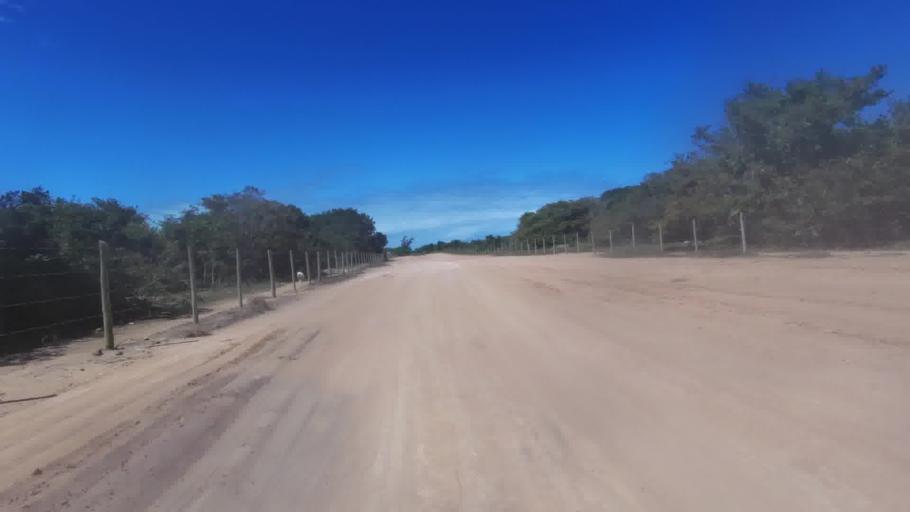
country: BR
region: Espirito Santo
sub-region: Marataizes
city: Marataizes
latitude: -21.1978
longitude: -40.9404
